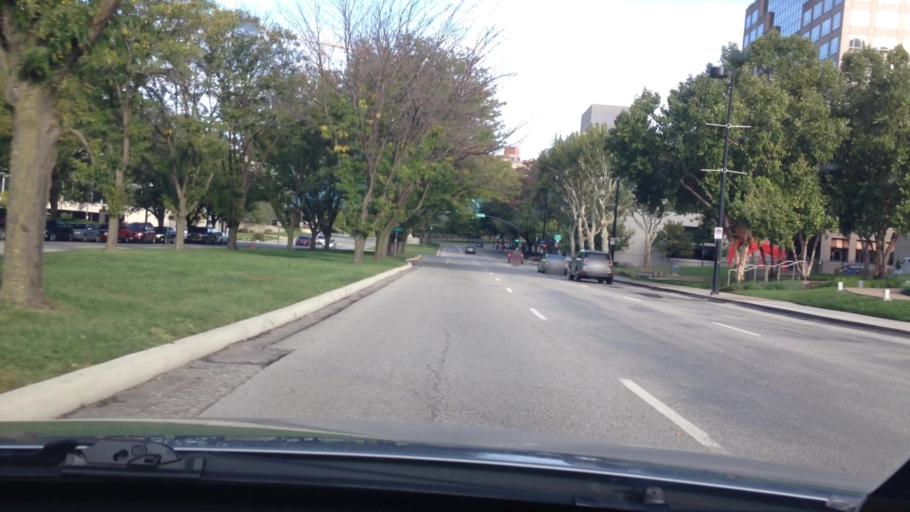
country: US
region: Missouri
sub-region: Jackson County
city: Kansas City
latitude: 39.0841
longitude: -94.5833
